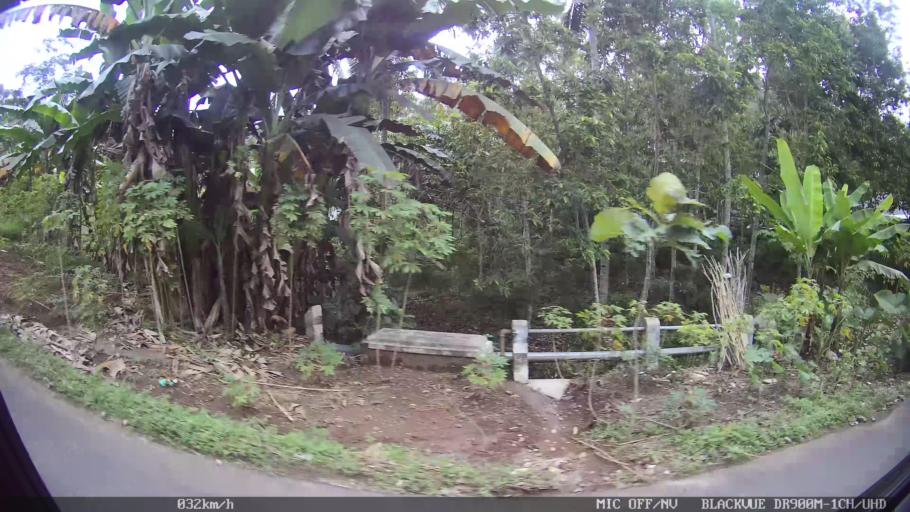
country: ID
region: Lampung
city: Kedaton
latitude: -5.3968
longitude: 105.1911
